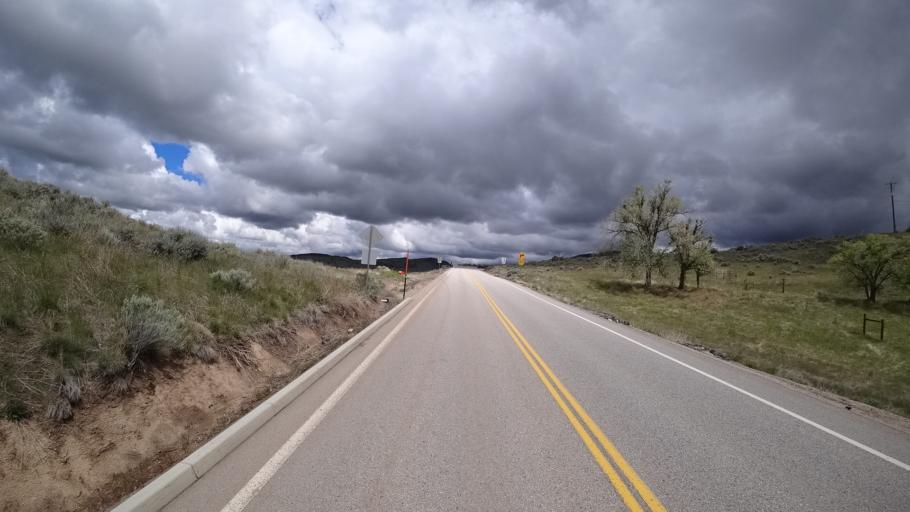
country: US
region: Idaho
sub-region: Ada County
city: Boise
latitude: 43.6934
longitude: -116.1784
